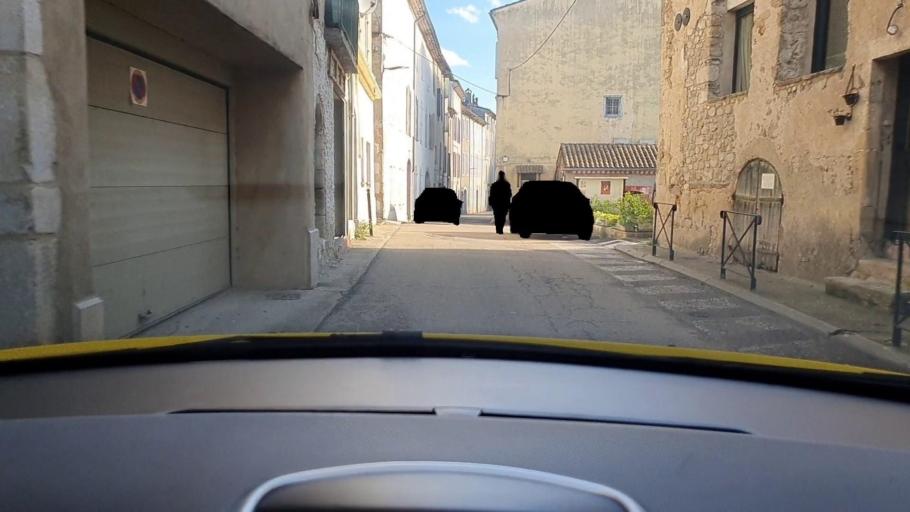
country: FR
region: Languedoc-Roussillon
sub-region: Departement du Gard
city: Lasalle
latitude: 44.0472
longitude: 3.8495
